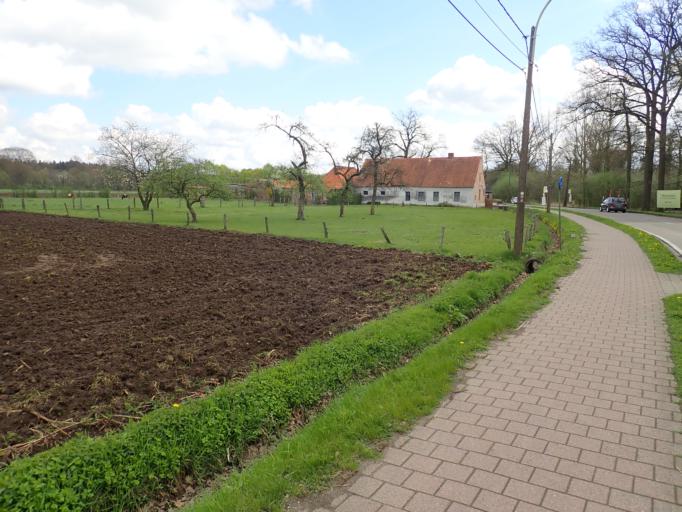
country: BE
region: Flanders
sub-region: Provincie Antwerpen
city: Grobbendonk
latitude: 51.1951
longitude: 4.7520
